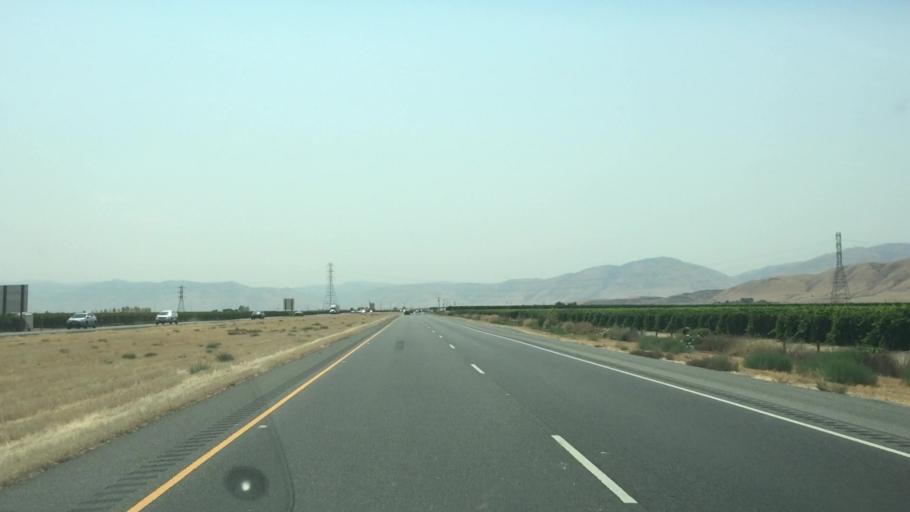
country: US
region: California
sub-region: Kern County
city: Weedpatch
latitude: 35.0532
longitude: -118.9929
